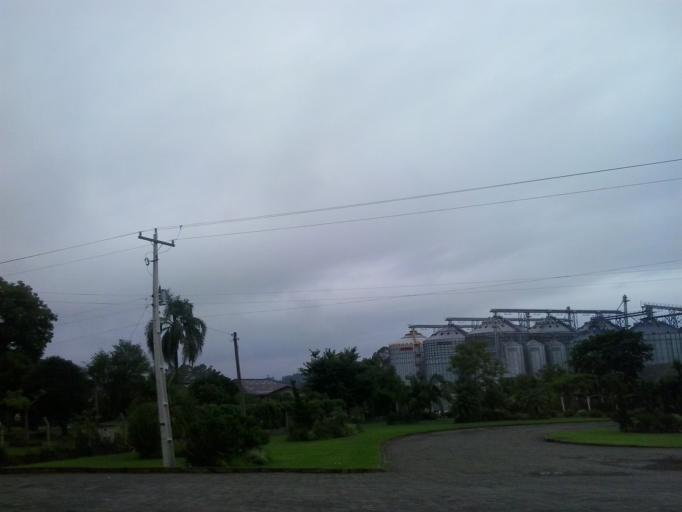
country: BR
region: Rio Grande do Sul
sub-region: Candelaria
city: Candelaria
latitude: -29.7151
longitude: -53.2490
